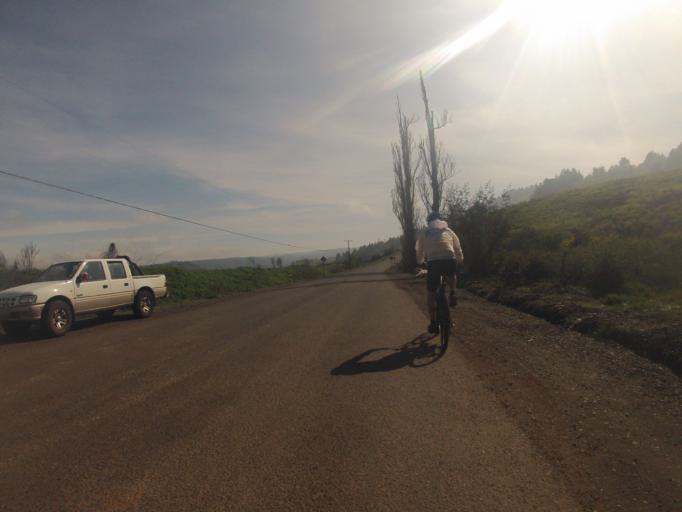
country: CL
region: Araucania
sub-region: Provincia de Cautin
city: Temuco
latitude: -38.7221
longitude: -72.6003
